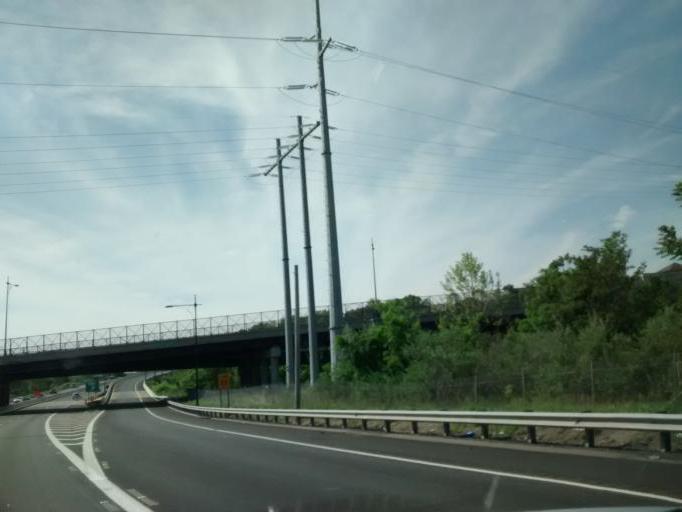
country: US
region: Massachusetts
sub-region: Worcester County
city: Millbury
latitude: 42.2028
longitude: -71.7767
